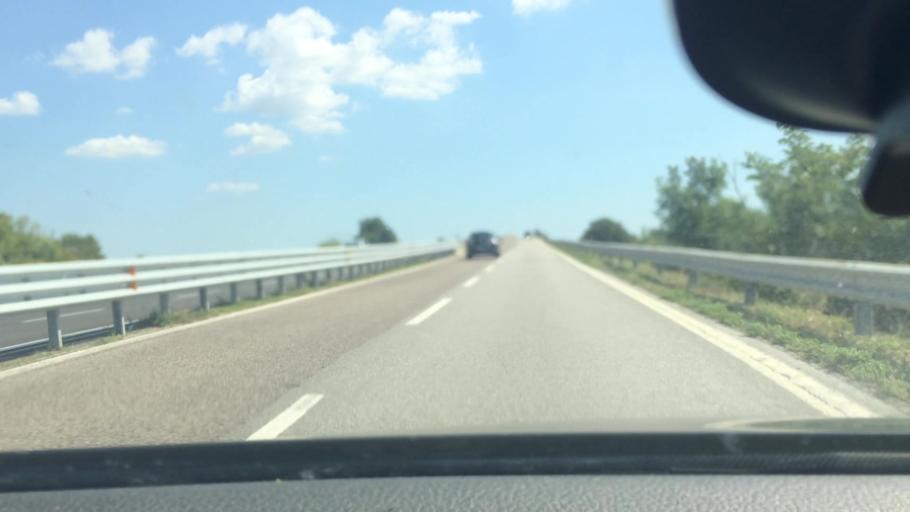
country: IT
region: Emilia-Romagna
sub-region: Provincia di Ferrara
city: Ostellato
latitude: 44.7557
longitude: 11.9499
